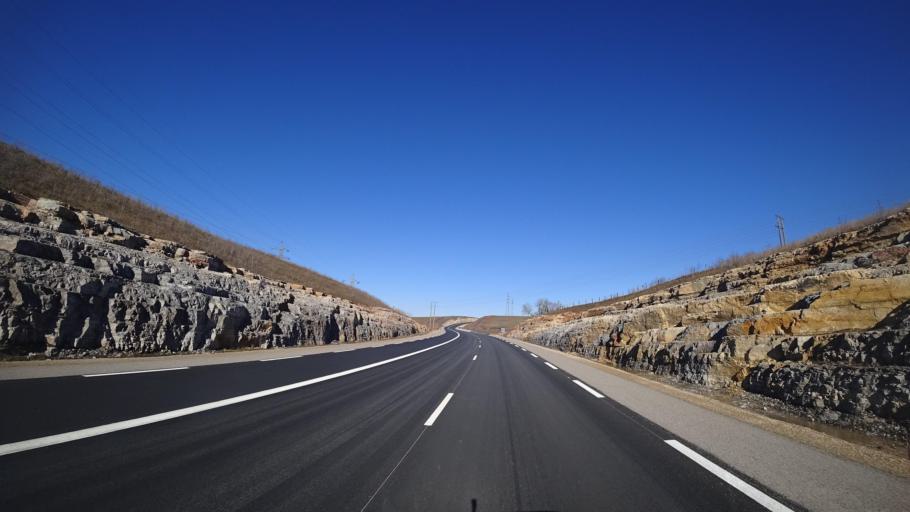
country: FR
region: Midi-Pyrenees
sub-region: Departement de l'Aveyron
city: Sebazac-Concoures
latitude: 44.3833
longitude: 2.6163
